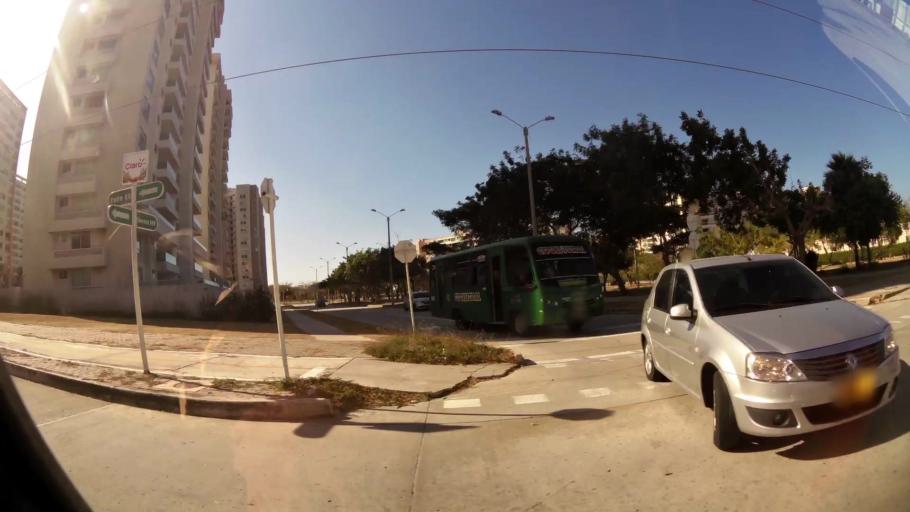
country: CO
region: Atlantico
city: Barranquilla
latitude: 11.0182
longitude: -74.8234
